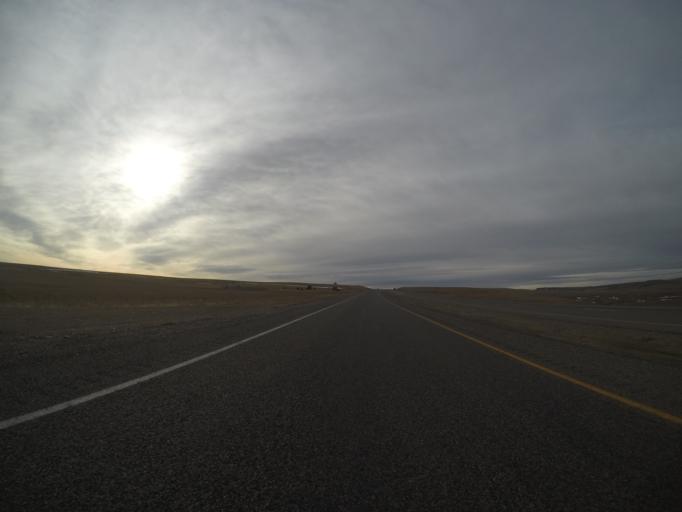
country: US
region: Montana
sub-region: Yellowstone County
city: Laurel
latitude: 45.5614
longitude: -108.8562
